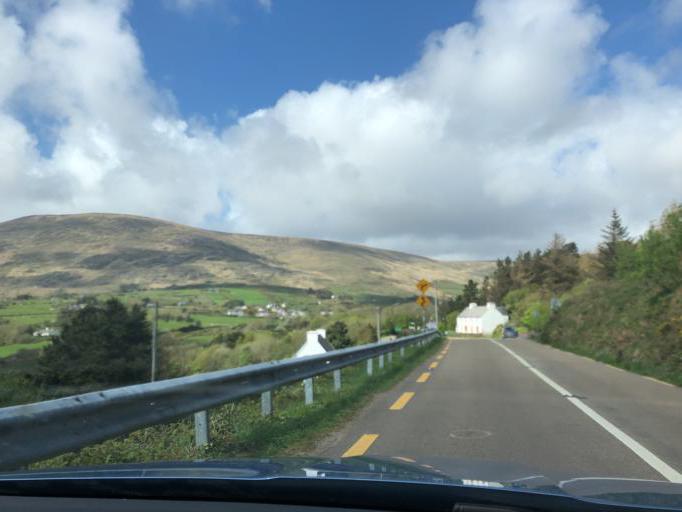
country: IE
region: Munster
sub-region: Ciarrai
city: Cahersiveen
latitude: 51.7640
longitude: -10.1001
